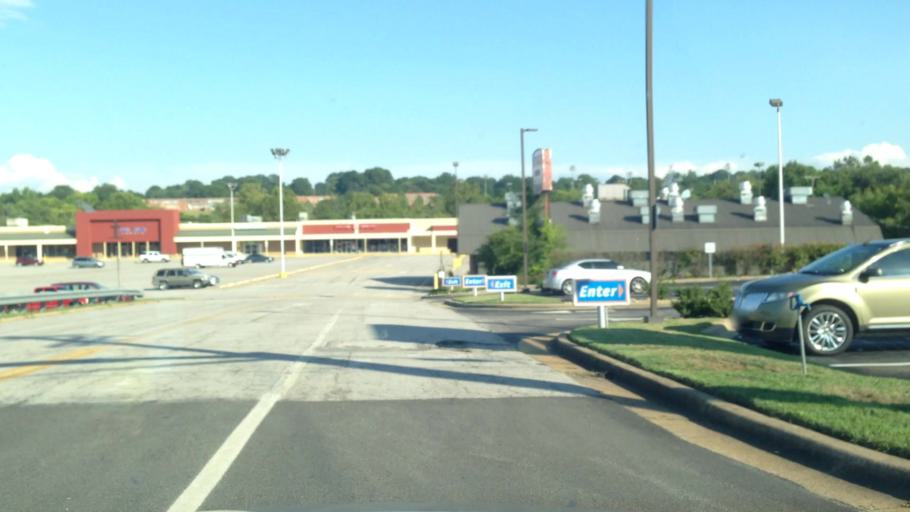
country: US
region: Virginia
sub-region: City of Danville
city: Danville
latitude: 36.5897
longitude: -79.4190
